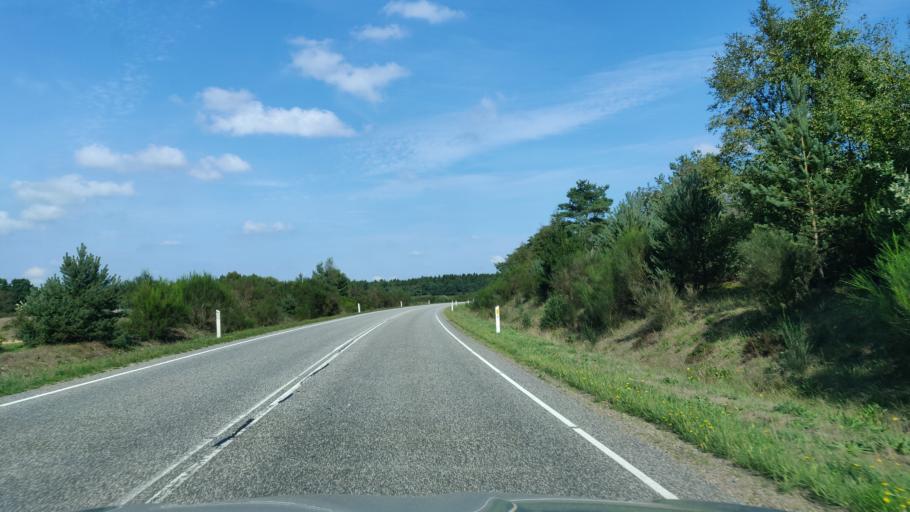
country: DK
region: Central Jutland
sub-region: Herning Kommune
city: Sunds
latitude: 56.3543
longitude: 8.9725
